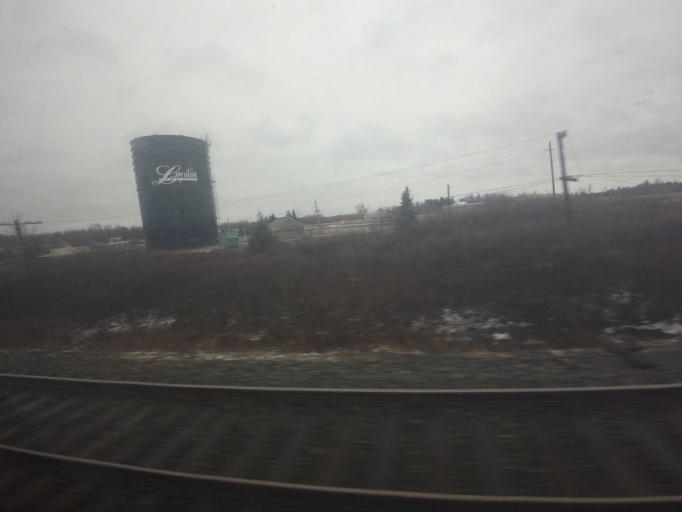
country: CA
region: Ontario
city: Kingston
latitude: 44.2315
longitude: -76.6760
